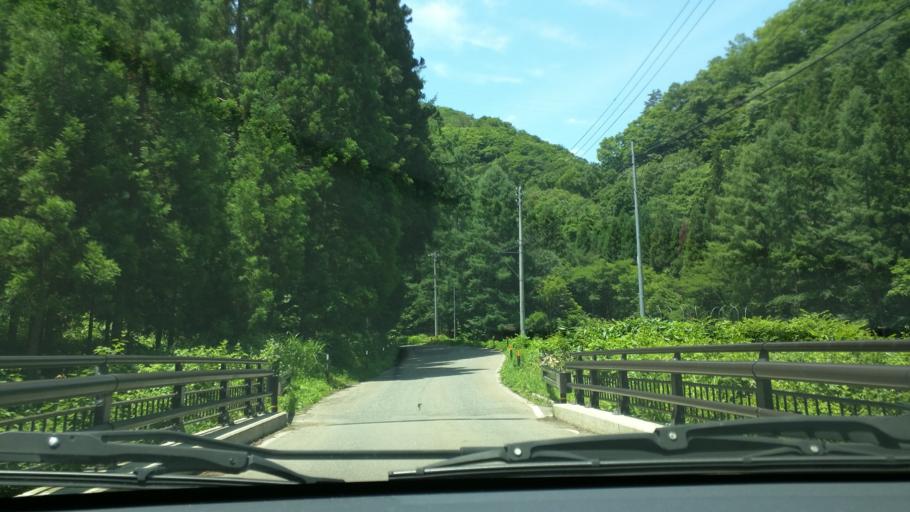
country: JP
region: Tochigi
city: Kuroiso
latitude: 37.2569
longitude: 139.7843
